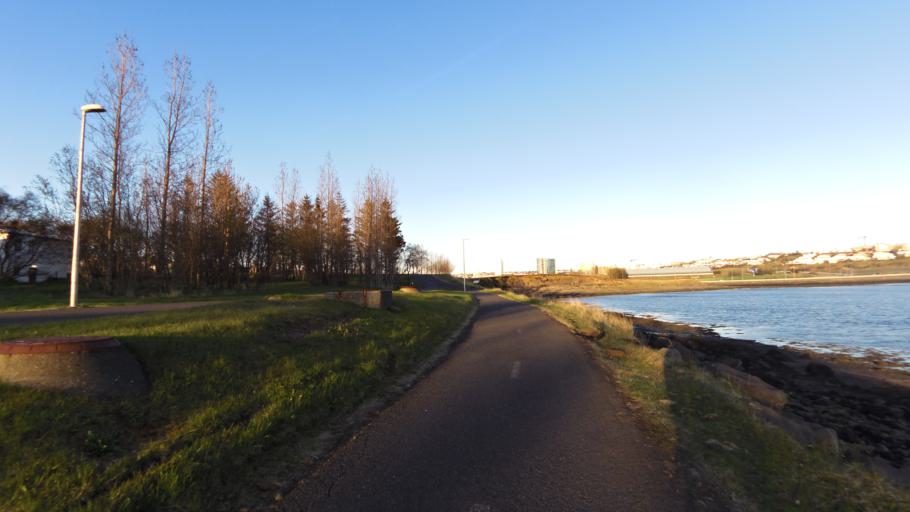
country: IS
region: Capital Region
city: Kopavogur
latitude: 64.1059
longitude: -21.9111
